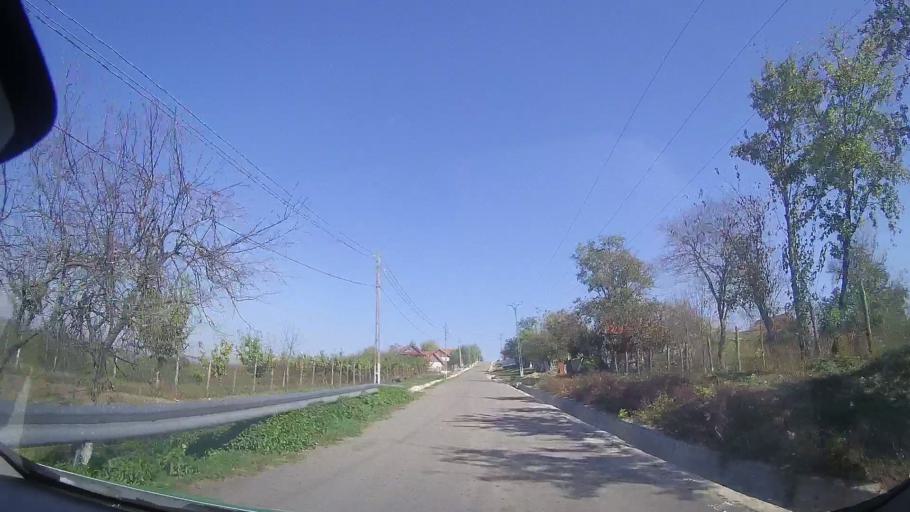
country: RO
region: Timis
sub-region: Comuna Ohaba Lunga
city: Ohaba Lunga
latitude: 45.9073
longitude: 21.9377
